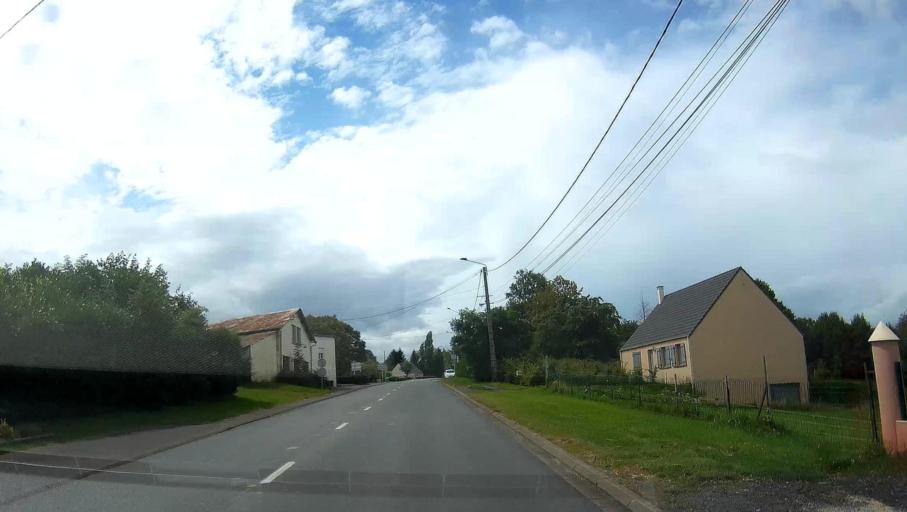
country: FR
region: Picardie
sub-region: Departement de l'Aisne
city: Rozoy-sur-Serre
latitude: 49.7059
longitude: 4.1174
